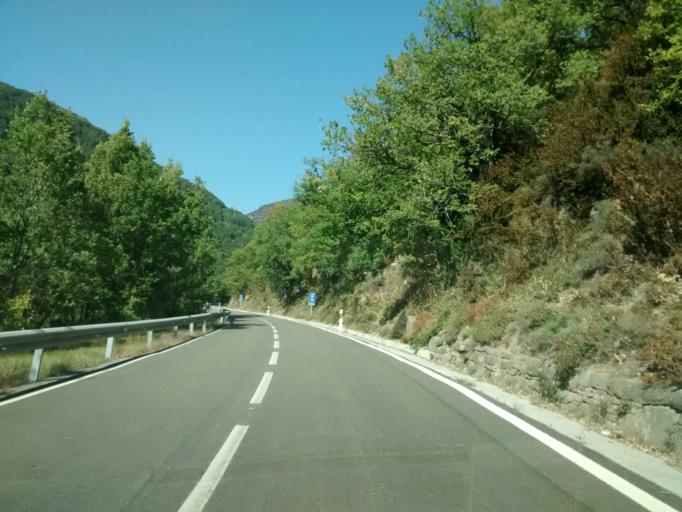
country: ES
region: Aragon
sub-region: Provincia de Huesca
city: Fiscal
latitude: 42.5305
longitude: -0.1368
